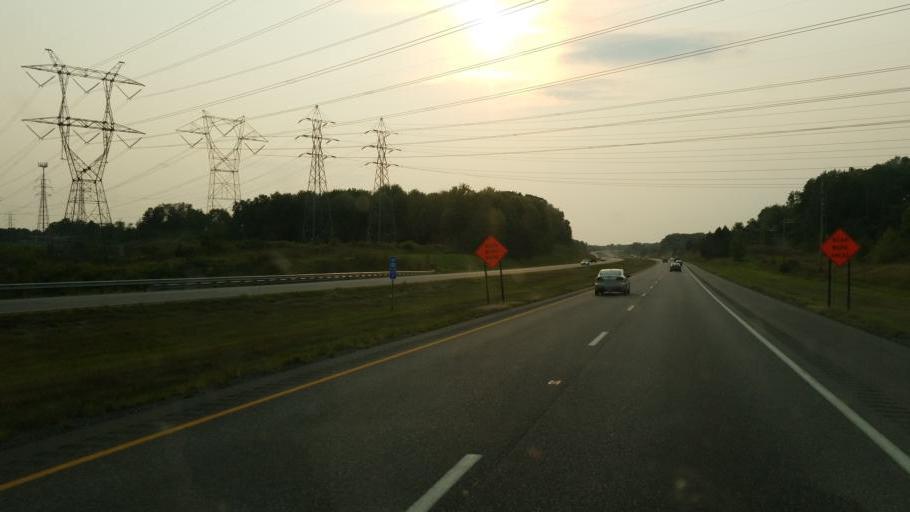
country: US
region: Ohio
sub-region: Cuyahoga County
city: Solon
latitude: 41.3893
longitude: -81.3981
